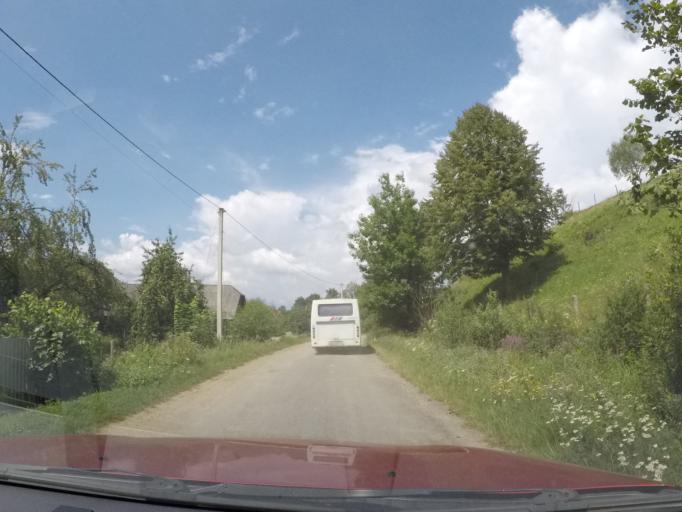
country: UA
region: Zakarpattia
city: Velykyi Bereznyi
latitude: 49.0242
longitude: 22.6080
